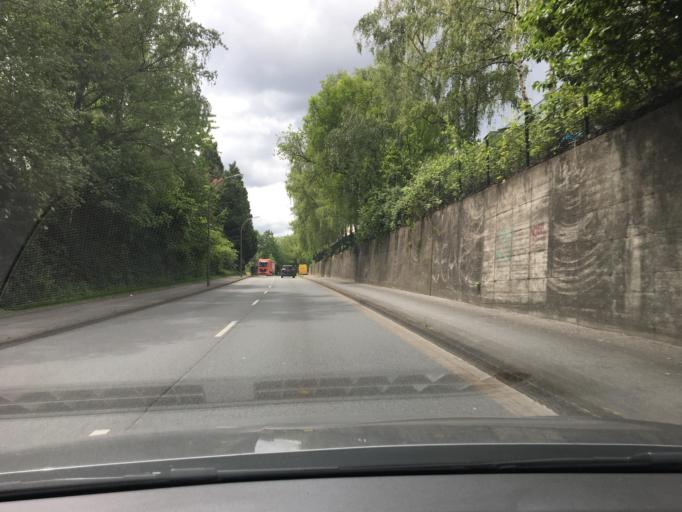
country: DE
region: North Rhine-Westphalia
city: Witten
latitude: 51.5121
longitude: 7.3741
